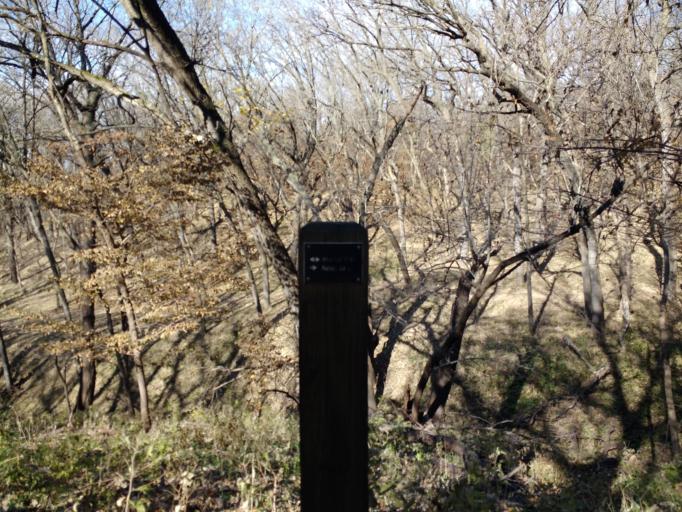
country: US
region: South Dakota
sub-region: Union County
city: North Sioux City
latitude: 42.5416
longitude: -96.4684
